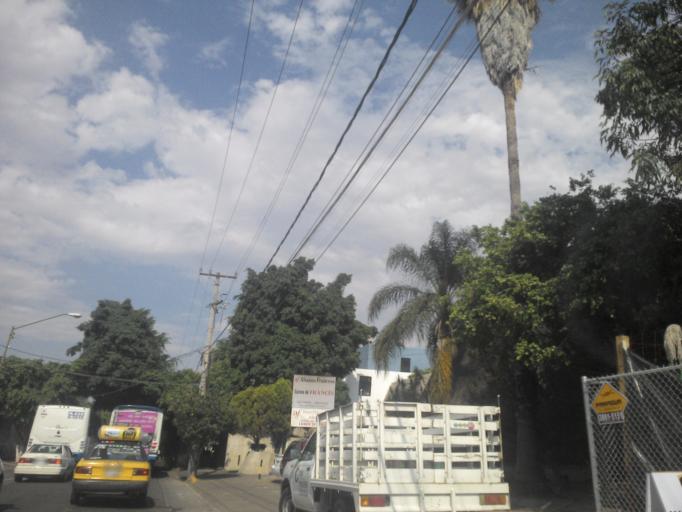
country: MX
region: Jalisco
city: Guadalajara
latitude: 20.6739
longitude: -103.3635
